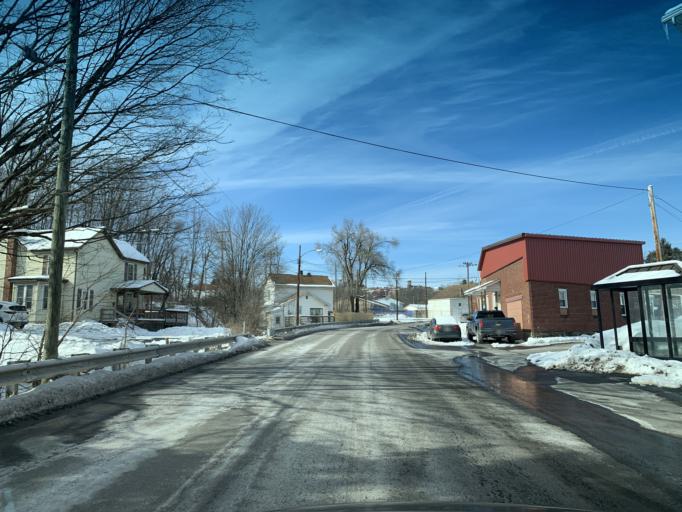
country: US
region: Maryland
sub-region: Allegany County
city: Frostburg
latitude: 39.6504
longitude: -78.9228
